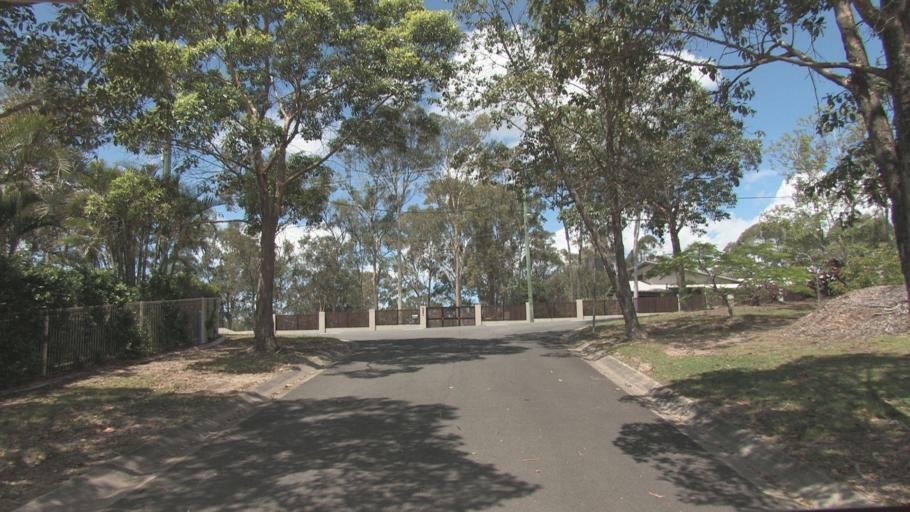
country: AU
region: Queensland
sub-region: Logan
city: Beenleigh
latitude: -27.6719
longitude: 153.2231
